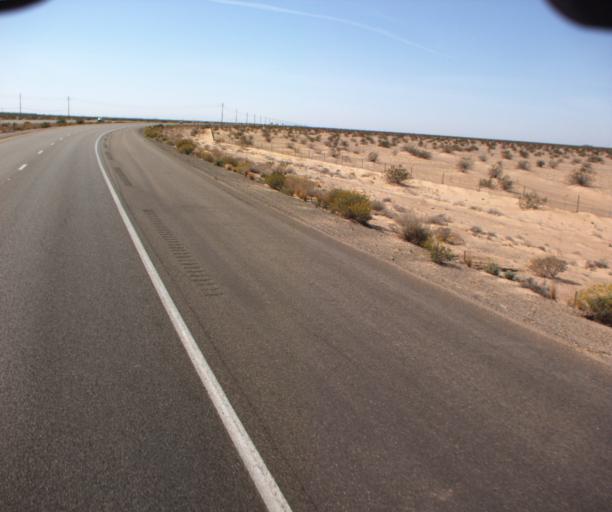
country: US
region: Arizona
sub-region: Yuma County
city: Somerton
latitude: 32.4955
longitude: -114.6589
